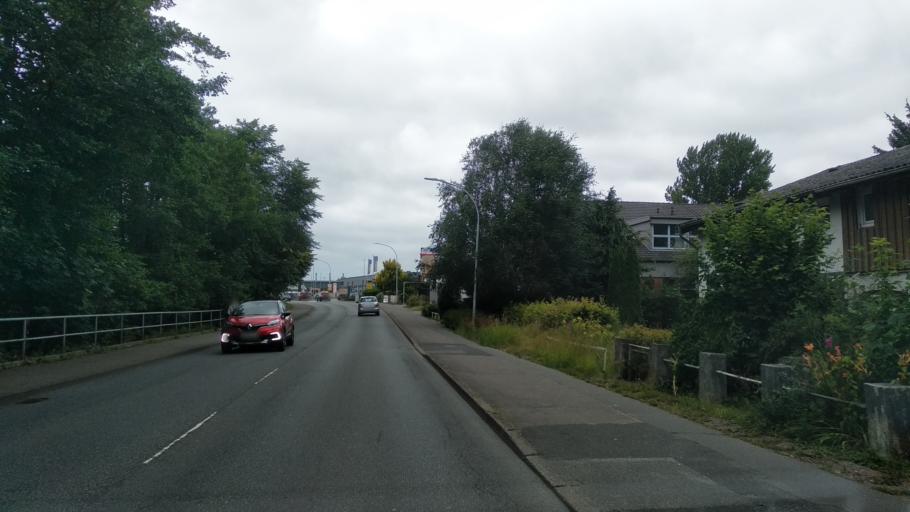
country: DE
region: Schleswig-Holstein
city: Neuberend
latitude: 54.5285
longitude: 9.5330
